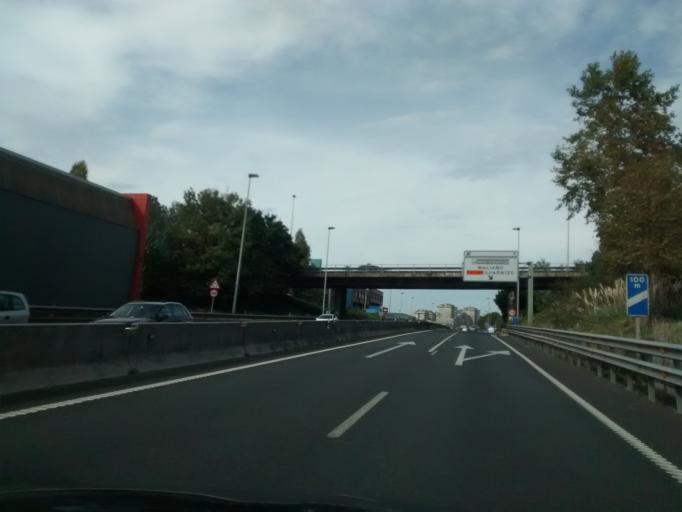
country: ES
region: Cantabria
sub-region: Provincia de Cantabria
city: El Astillero
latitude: 43.4107
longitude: -3.8344
